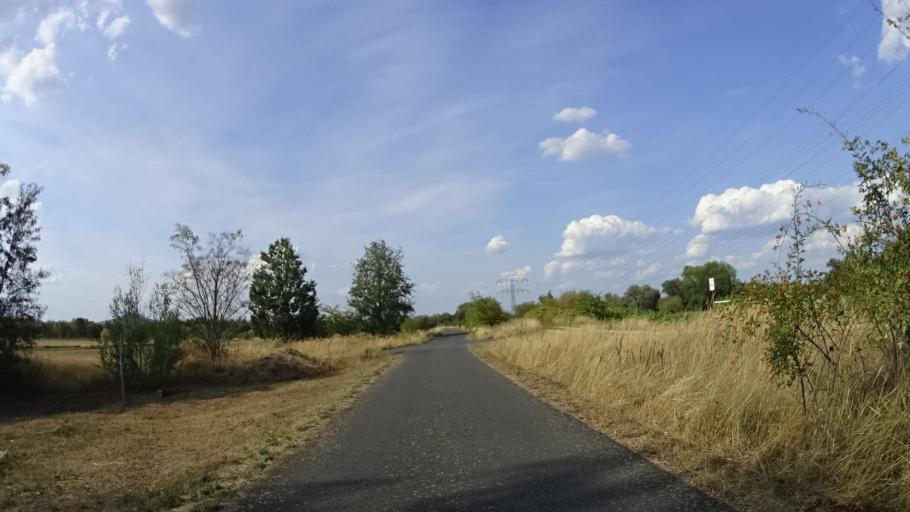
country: DE
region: Saxony
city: Goerlitz
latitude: 51.0828
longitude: 14.9748
